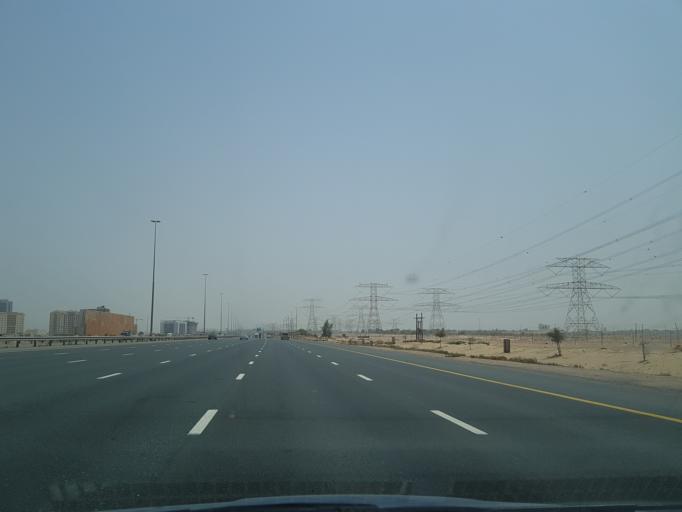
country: AE
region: Dubai
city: Dubai
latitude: 25.0779
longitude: 55.3785
